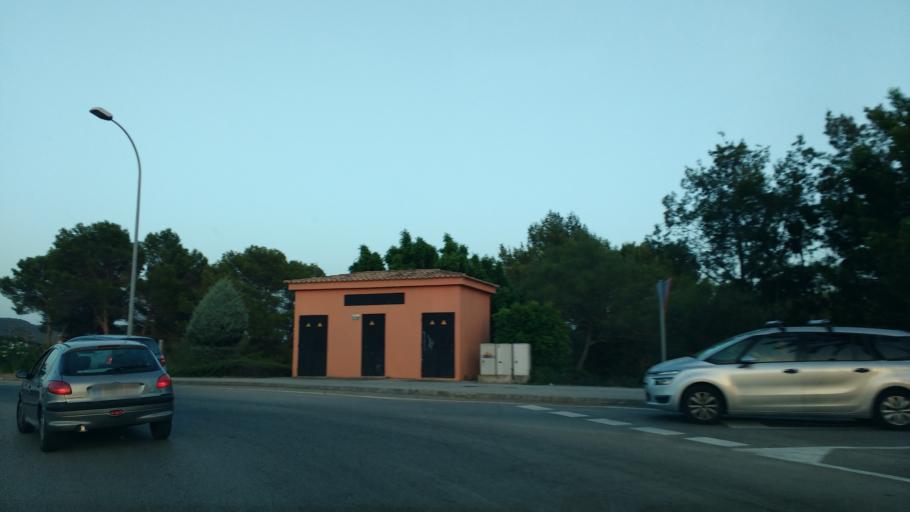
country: ES
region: Balearic Islands
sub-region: Illes Balears
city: Marratxi
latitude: 39.6315
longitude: 2.7352
